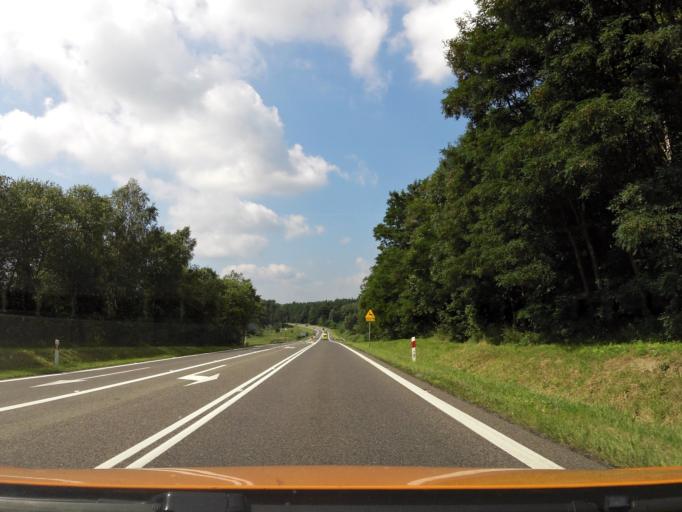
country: PL
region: West Pomeranian Voivodeship
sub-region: Powiat goleniowski
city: Mosty
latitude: 53.6156
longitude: 14.9280
